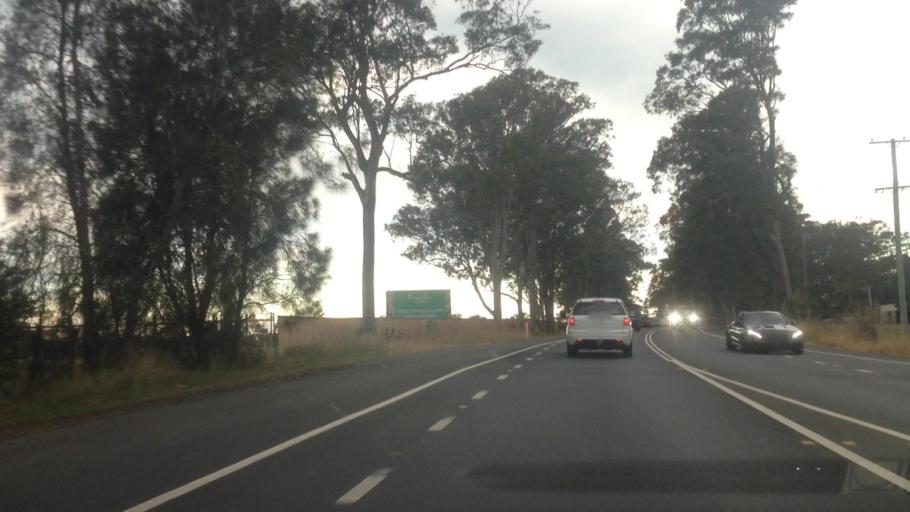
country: AU
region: New South Wales
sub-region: Wyong Shire
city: Tuggerawong
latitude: -33.2630
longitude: 151.4665
